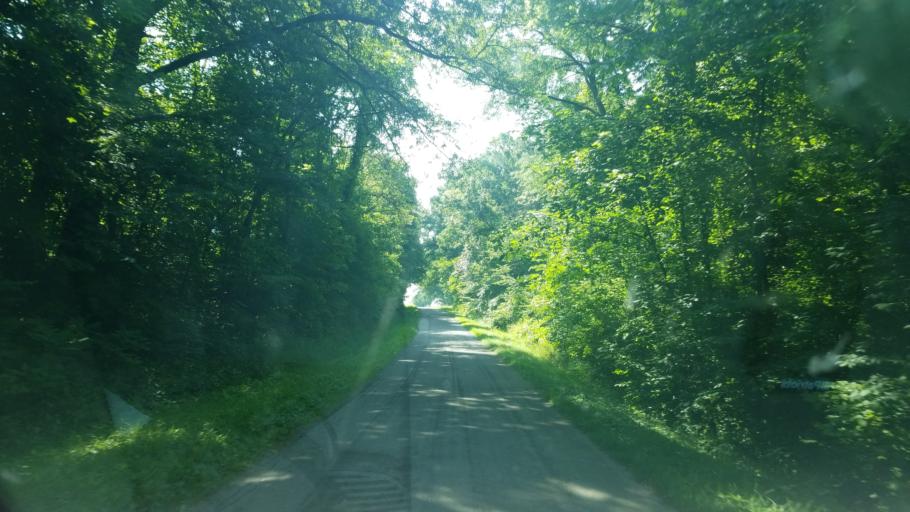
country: US
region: Ohio
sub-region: Wyandot County
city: Upper Sandusky
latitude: 40.9023
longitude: -83.2493
